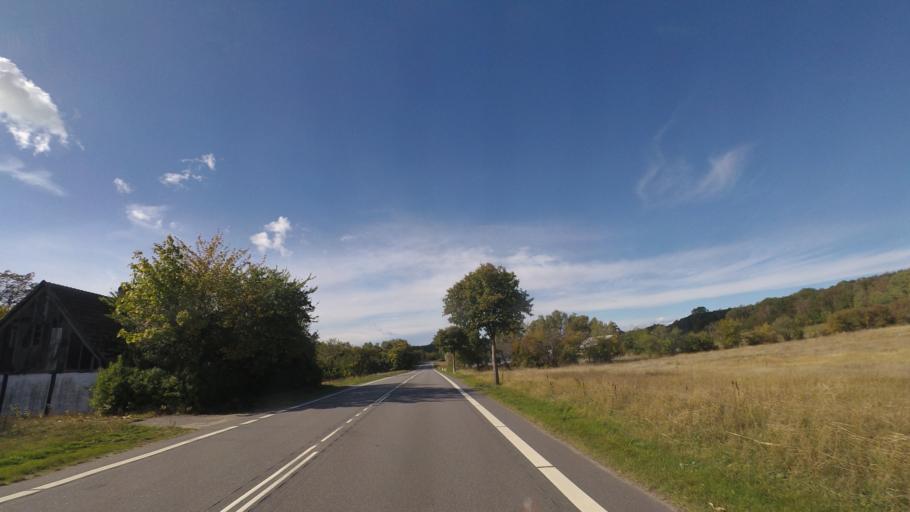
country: DK
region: Capital Region
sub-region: Bornholm Kommune
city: Ronne
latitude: 55.0788
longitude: 14.7639
